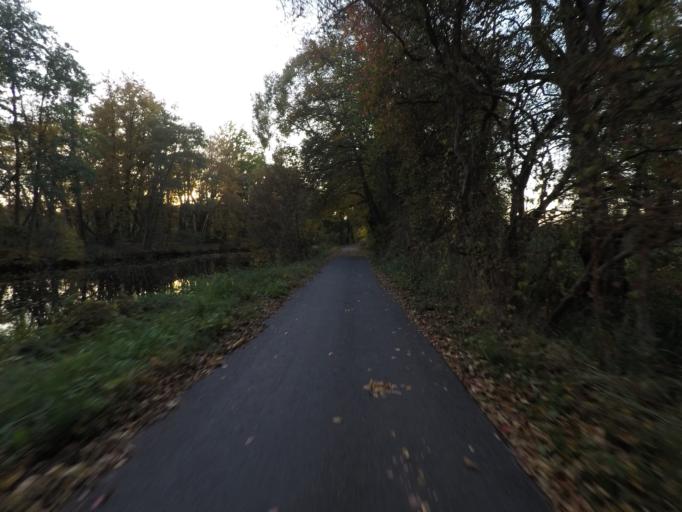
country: DE
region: Brandenburg
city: Melchow
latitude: 52.8453
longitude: 13.7000
